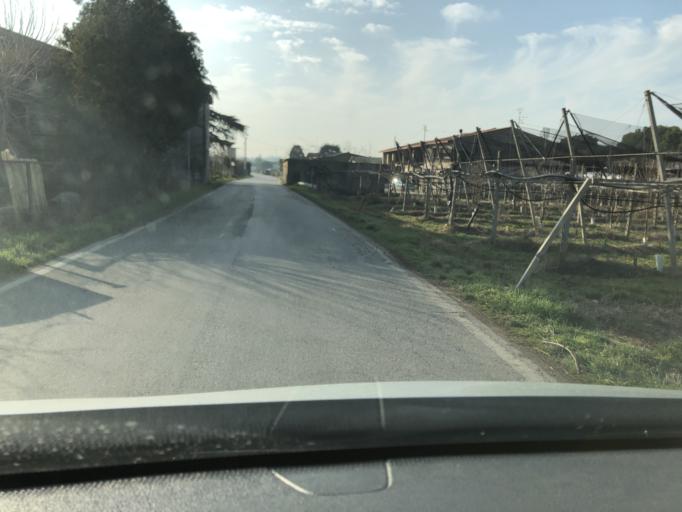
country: IT
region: Veneto
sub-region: Provincia di Verona
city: Caselle
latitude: 45.4128
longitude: 10.8728
